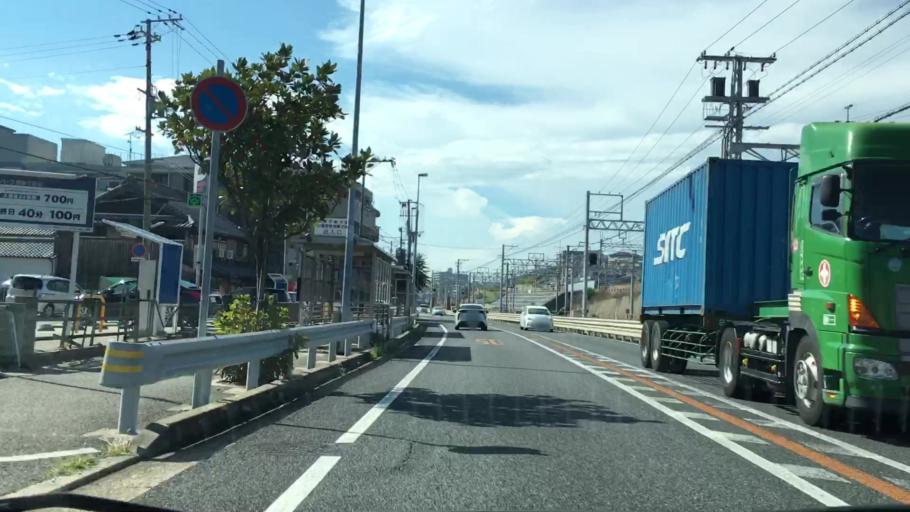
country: JP
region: Hyogo
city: Akashi
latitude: 34.6388
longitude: 135.0276
